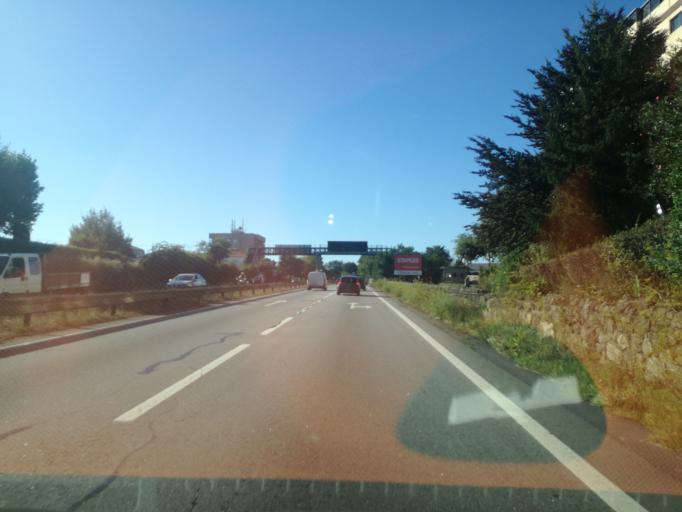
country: PT
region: Porto
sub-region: Matosinhos
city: Sao Mamede de Infesta
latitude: 41.1876
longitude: -8.6255
